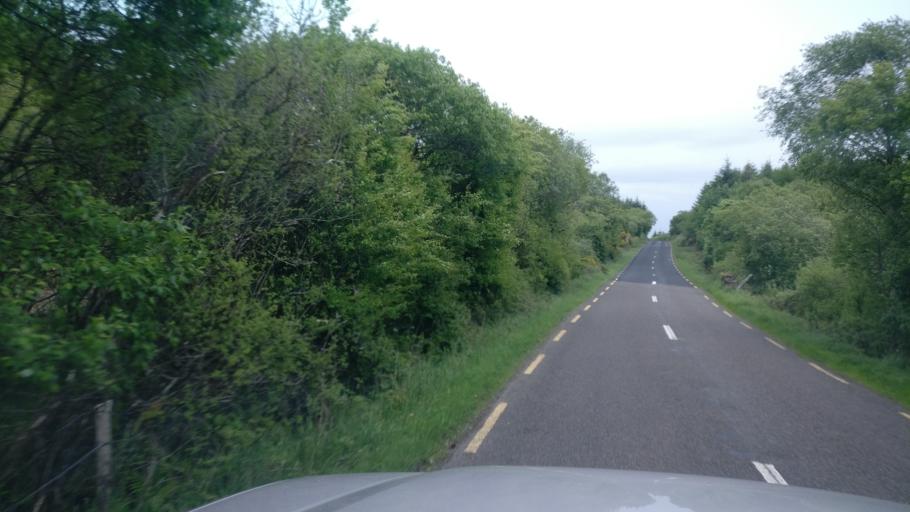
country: IE
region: Connaught
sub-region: County Galway
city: Loughrea
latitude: 53.0762
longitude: -8.5568
